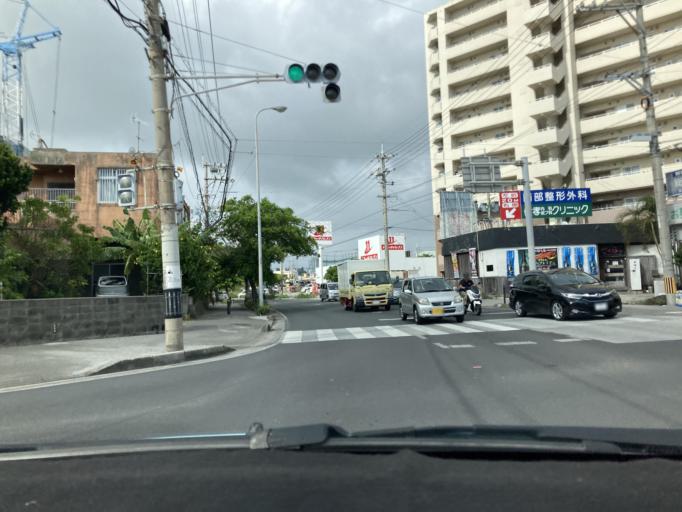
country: JP
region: Okinawa
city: Itoman
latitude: 26.1461
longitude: 127.6735
